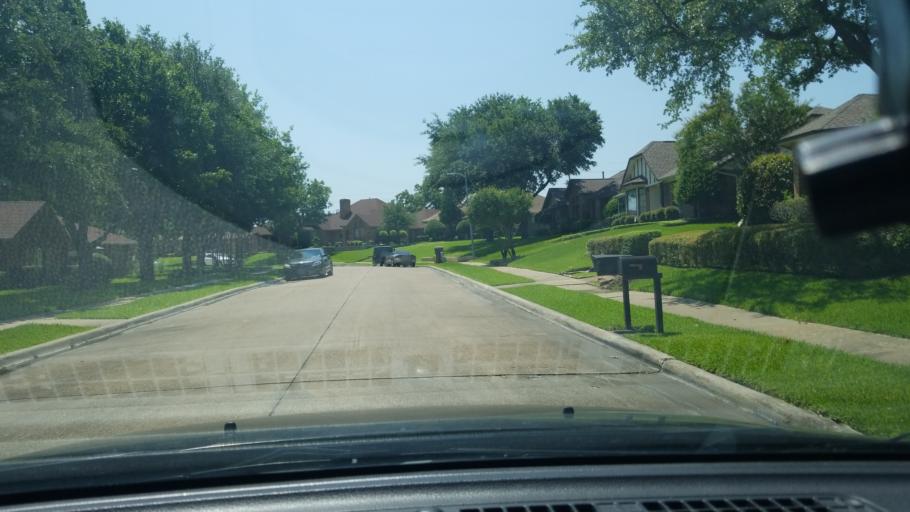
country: US
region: Texas
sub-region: Dallas County
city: Mesquite
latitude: 32.8255
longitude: -96.6154
